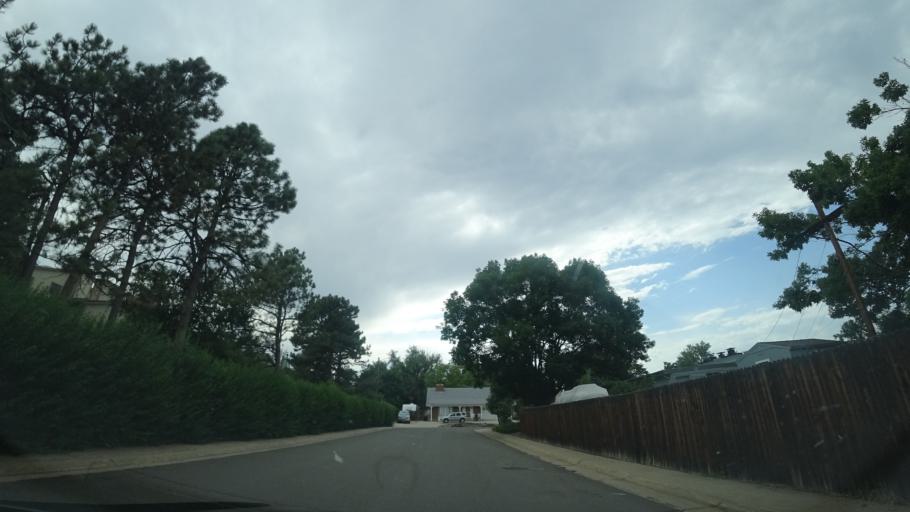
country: US
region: Colorado
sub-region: Jefferson County
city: Lakewood
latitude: 39.7149
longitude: -105.0983
